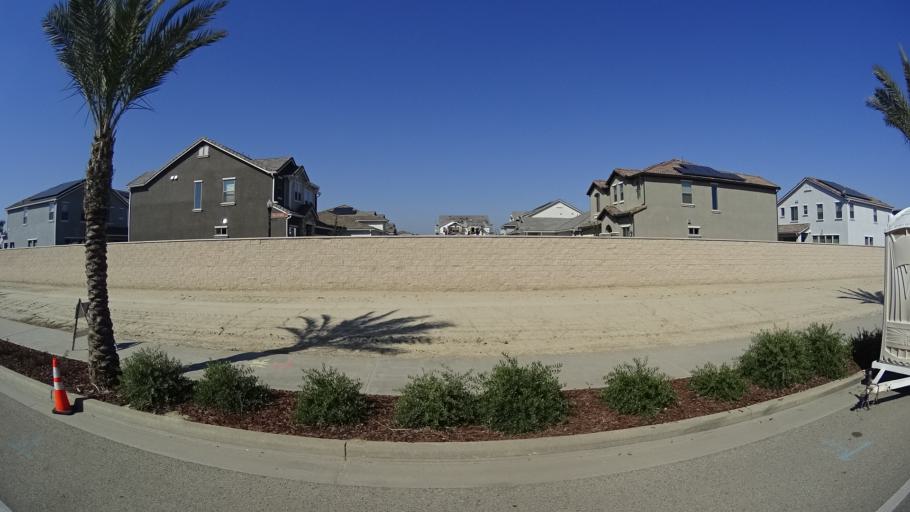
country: US
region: California
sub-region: Fresno County
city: Clovis
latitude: 36.9017
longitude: -119.7569
